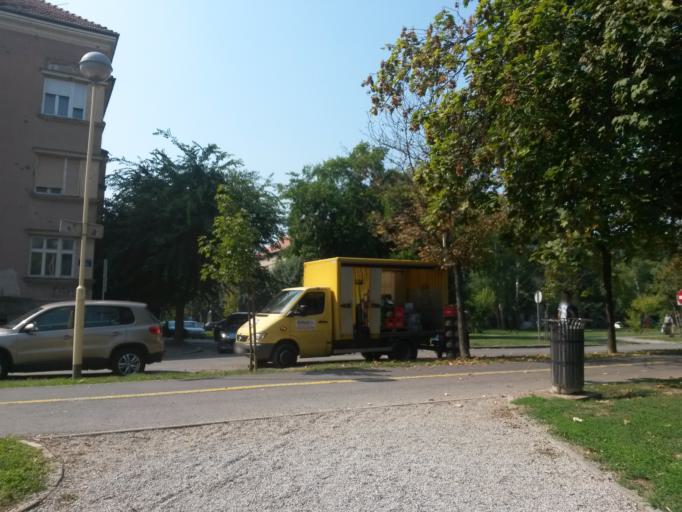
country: HR
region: Osjecko-Baranjska
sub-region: Grad Osijek
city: Osijek
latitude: 45.5583
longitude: 18.6916
